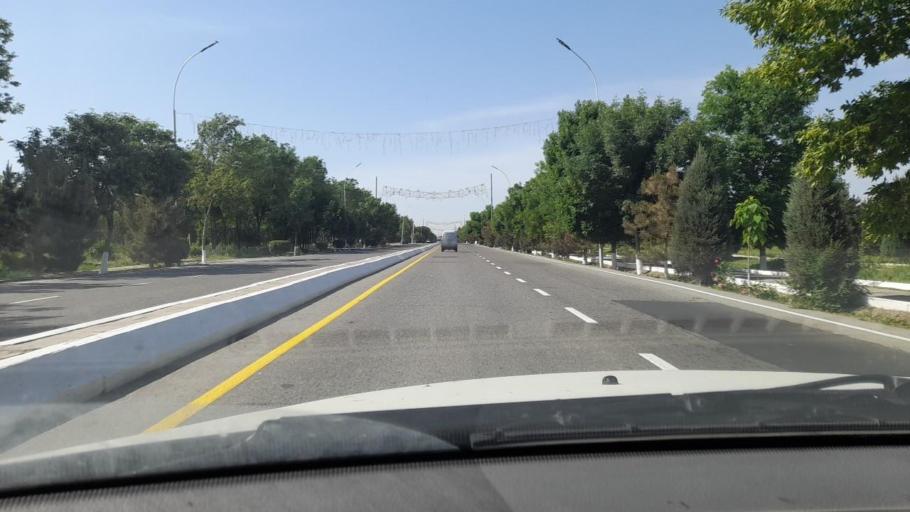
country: UZ
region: Bukhara
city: Bukhara
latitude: 39.7960
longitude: 64.4349
